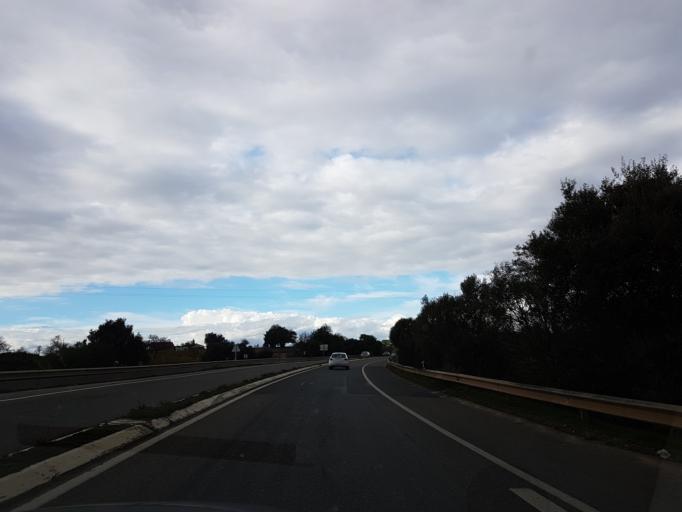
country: PT
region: Faro
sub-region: Albufeira
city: Ferreiras
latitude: 37.1195
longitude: -8.2472
